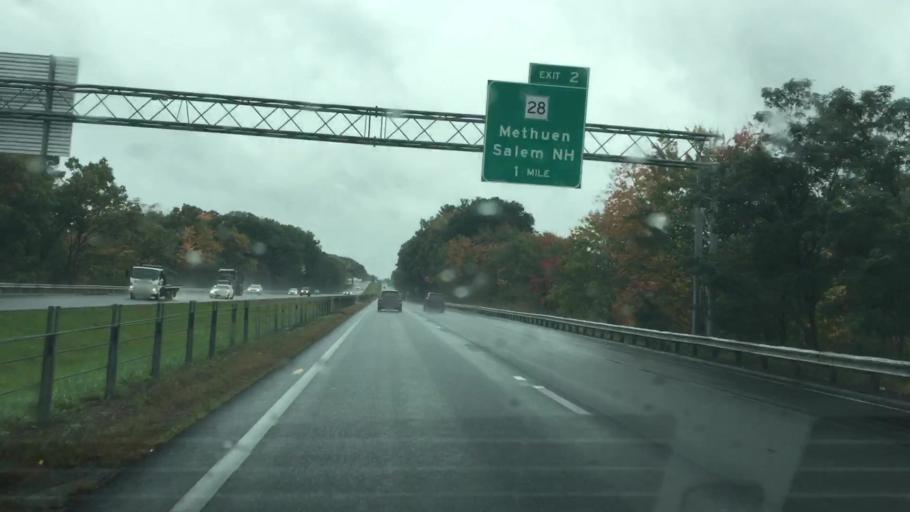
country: US
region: Massachusetts
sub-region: Essex County
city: Methuen
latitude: 42.7411
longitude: -71.1722
